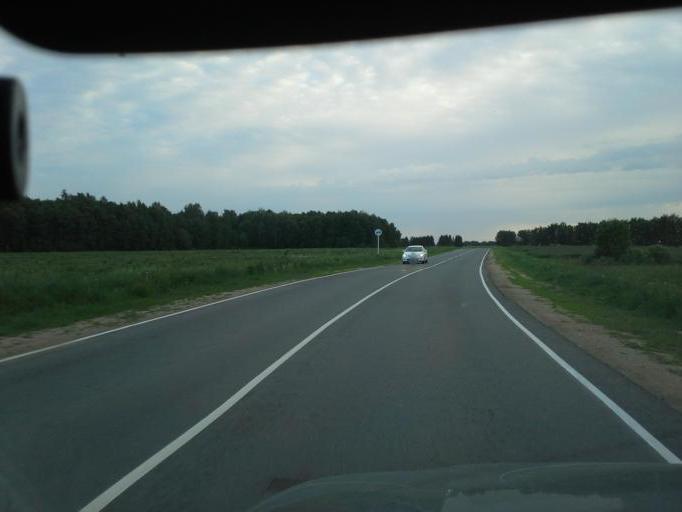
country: RU
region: Ivanovo
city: Gavrilov Posad
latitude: 56.5850
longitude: 40.2208
